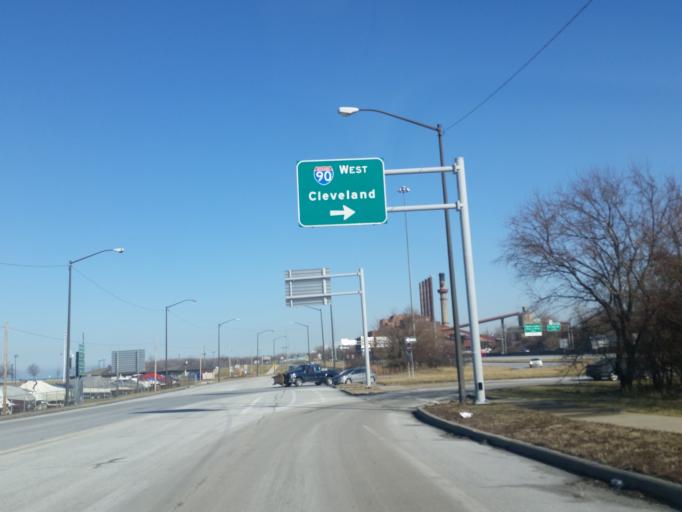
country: US
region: Ohio
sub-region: Cuyahoga County
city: Bratenahl
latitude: 41.5321
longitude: -81.6506
